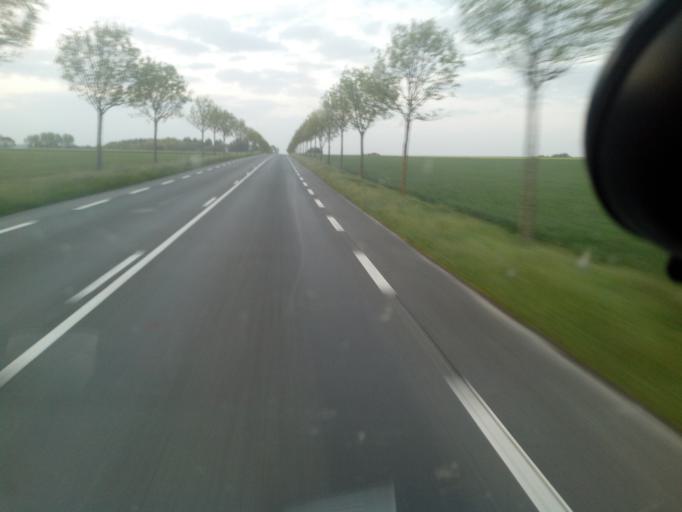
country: FR
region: Nord-Pas-de-Calais
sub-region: Departement du Pas-de-Calais
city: Hesdin
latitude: 50.3438
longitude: 2.0314
